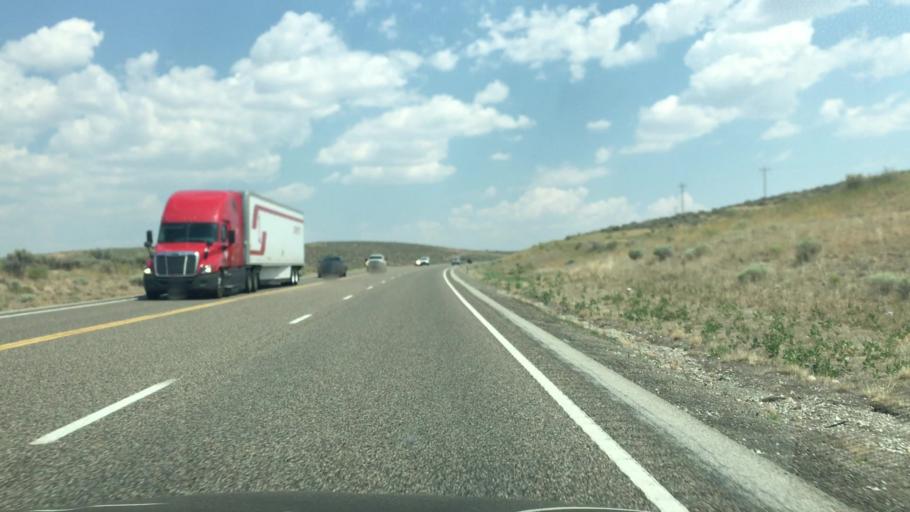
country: US
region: Nevada
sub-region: Elko County
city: Wells
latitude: 41.1842
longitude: -114.8747
